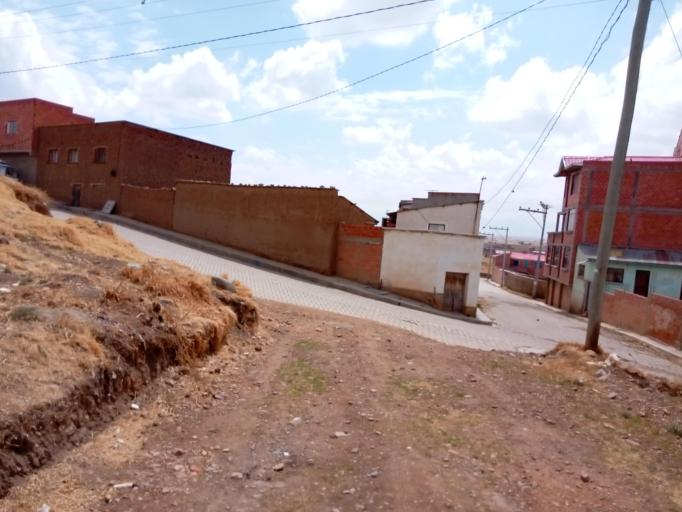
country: BO
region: La Paz
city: Batallas
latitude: -16.3975
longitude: -68.4793
